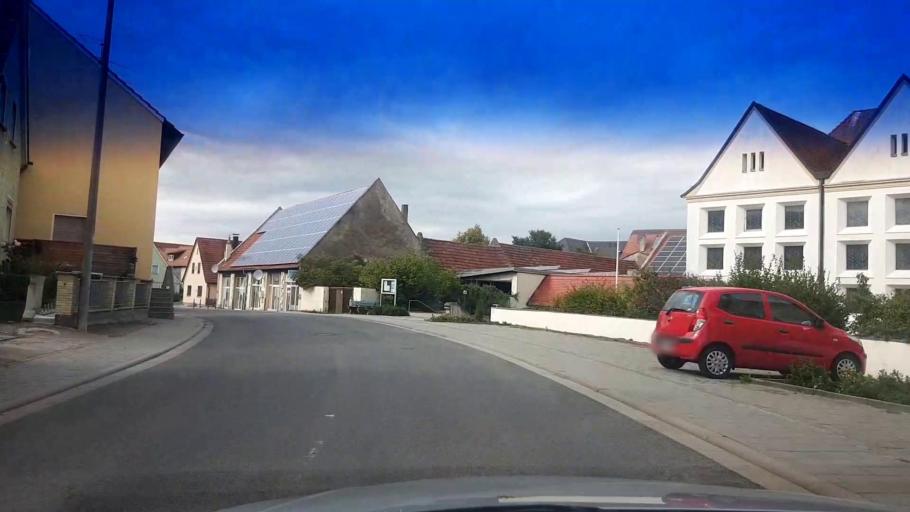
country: DE
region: Bavaria
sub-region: Upper Franconia
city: Frensdorf
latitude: 49.8161
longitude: 10.8662
